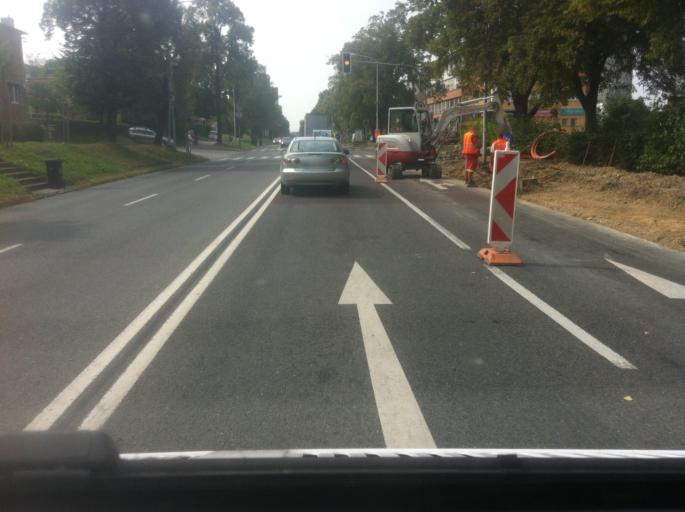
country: CZ
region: Zlin
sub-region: Okres Zlin
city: Zlin
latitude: 49.2254
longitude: 17.6825
